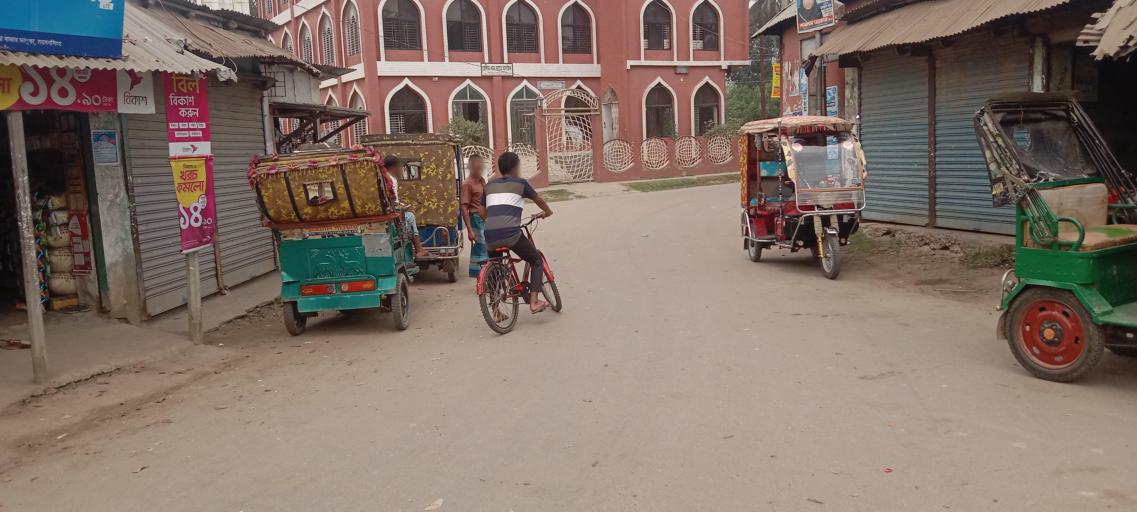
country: BD
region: Dhaka
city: Gafargaon
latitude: 24.4621
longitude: 90.4104
